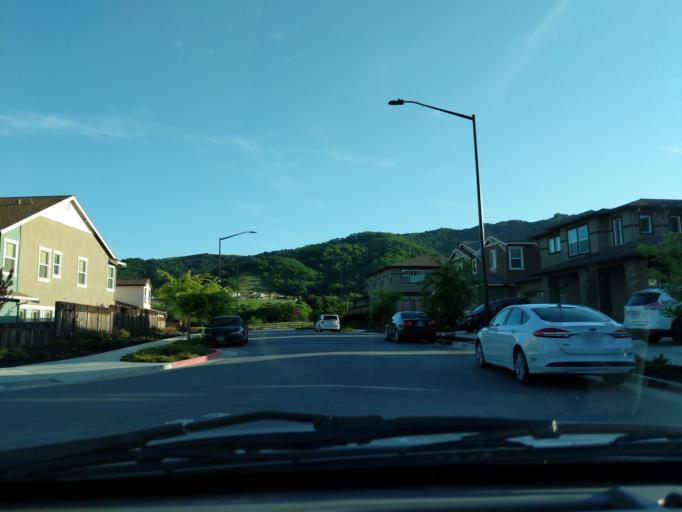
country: US
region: California
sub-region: Santa Clara County
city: Gilroy
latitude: 36.9879
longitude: -121.5831
